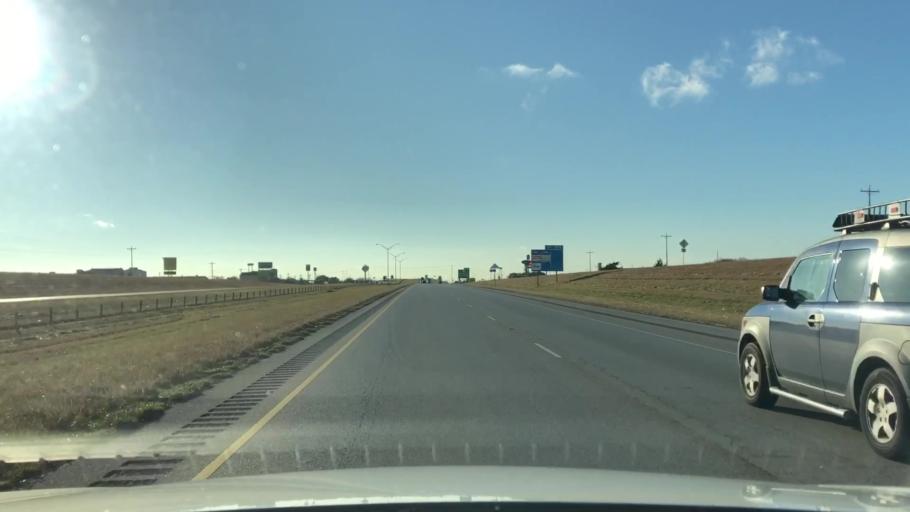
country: US
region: Texas
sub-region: Fayette County
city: Schulenburg
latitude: 29.6959
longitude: -96.8918
